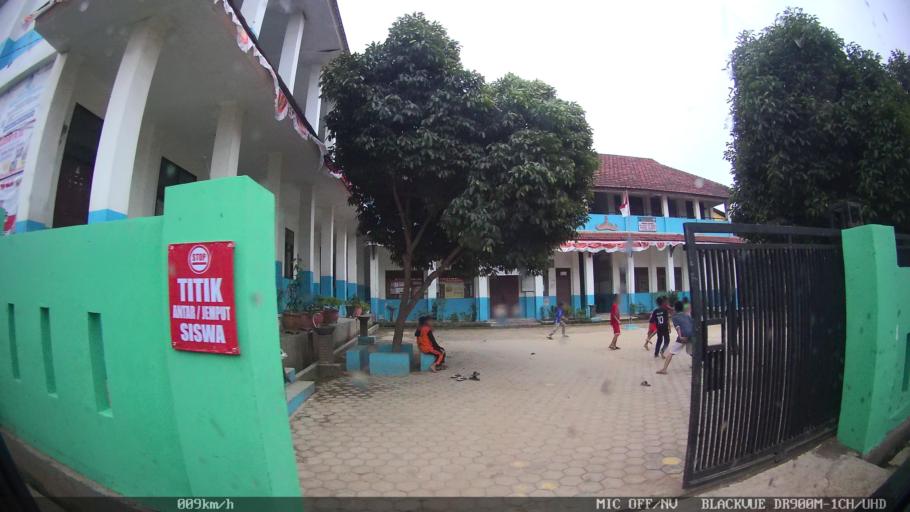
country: ID
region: Lampung
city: Kedaton
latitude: -5.3964
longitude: 105.2805
